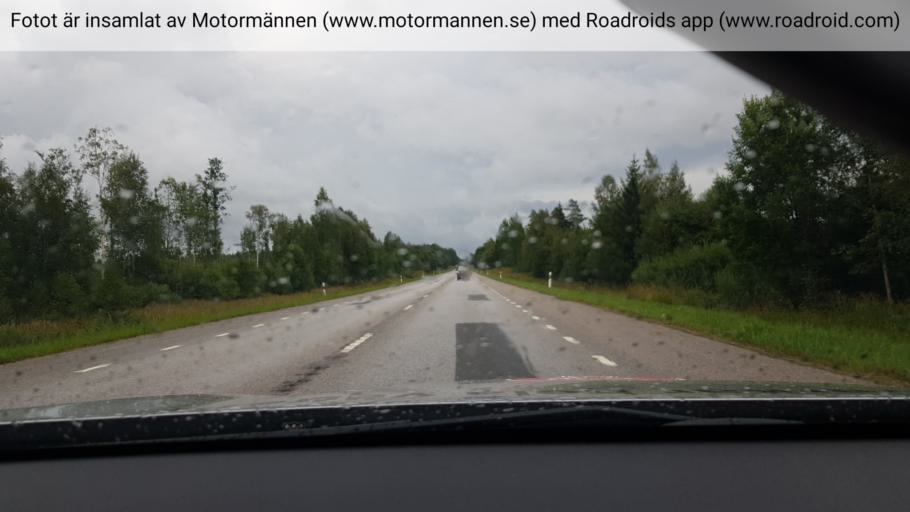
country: SE
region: Uppsala
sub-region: Alvkarleby Kommun
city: AElvkarleby
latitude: 60.5513
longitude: 17.4996
